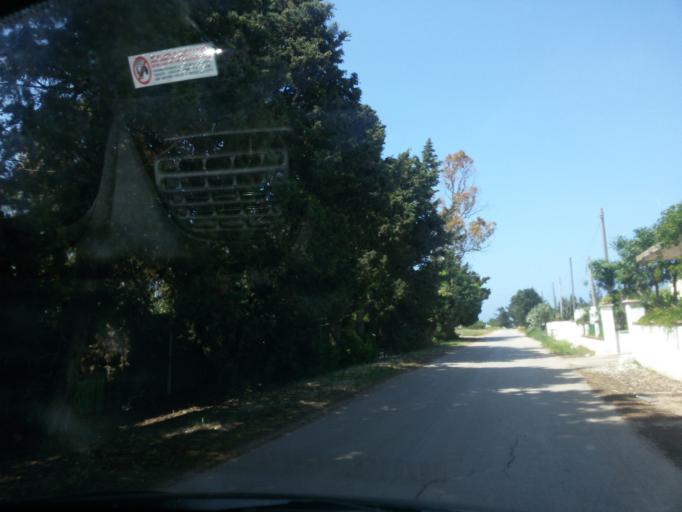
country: IT
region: Apulia
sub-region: Provincia di Brindisi
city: Brindisi
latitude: 40.6641
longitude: 17.8611
